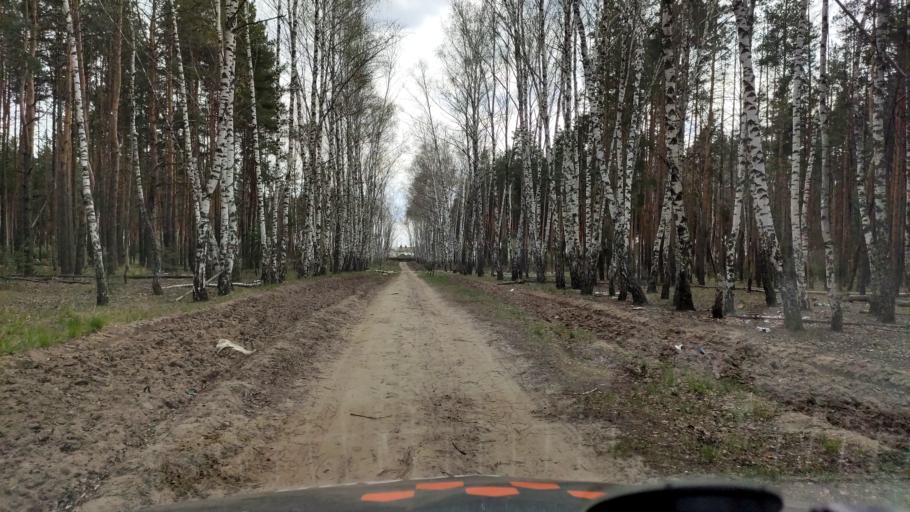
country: RU
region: Voronezj
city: Somovo
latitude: 51.7456
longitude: 39.2755
